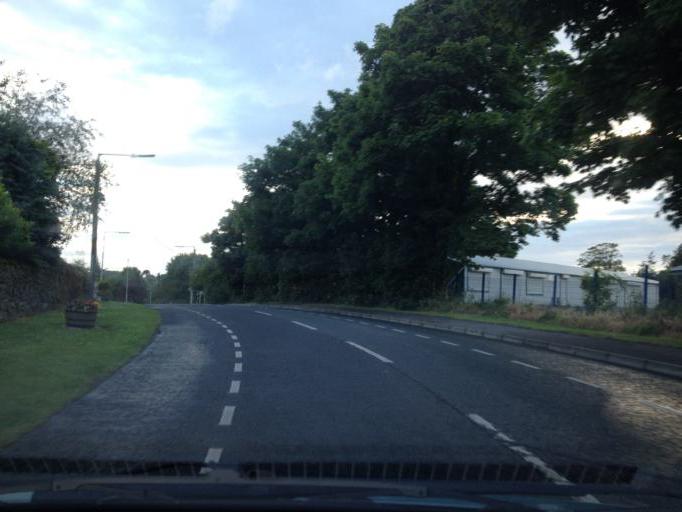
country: IE
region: Connaught
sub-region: Sligo
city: Sligo
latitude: 54.2614
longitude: -8.4590
